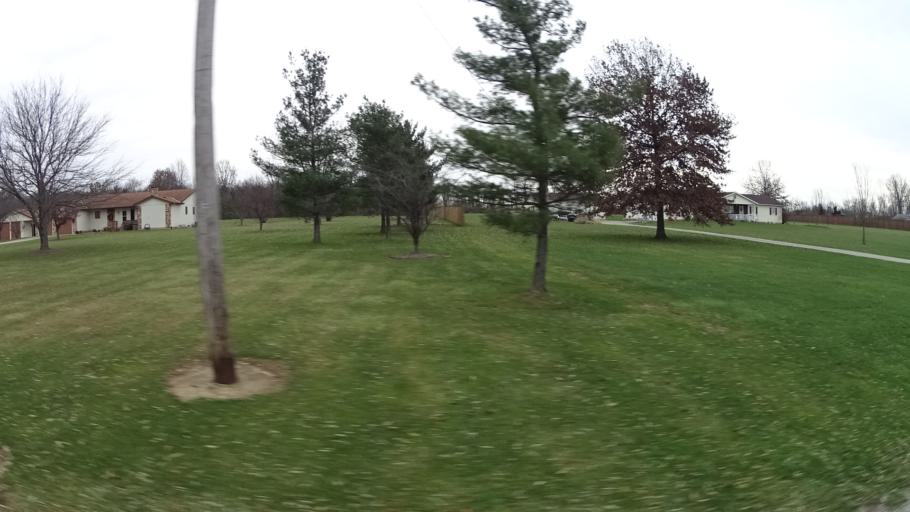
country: US
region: Ohio
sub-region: Lorain County
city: Lagrange
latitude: 41.1735
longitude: -82.0834
